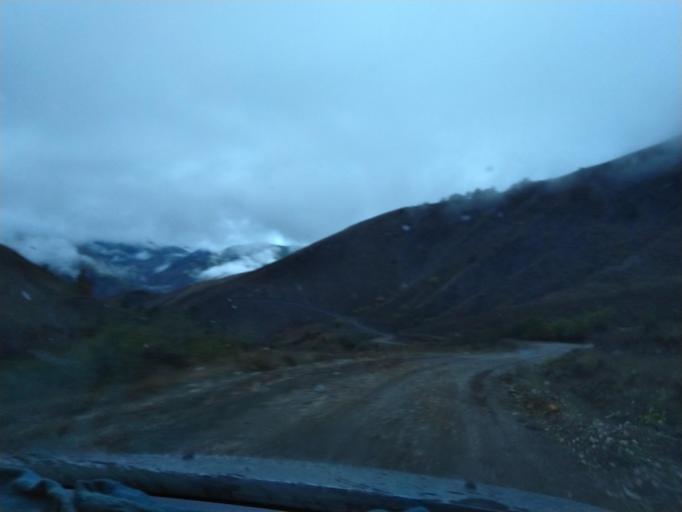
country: RU
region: North Ossetia
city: Tarskoye
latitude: 42.8232
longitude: 44.9712
